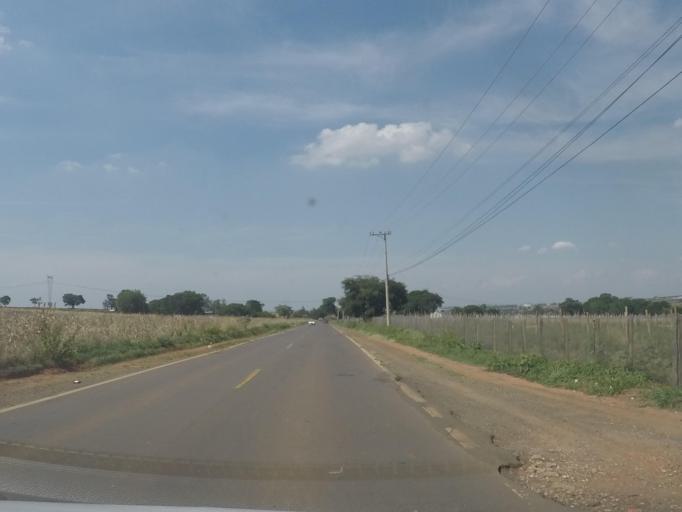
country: BR
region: Sao Paulo
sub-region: Sumare
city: Sumare
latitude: -22.8696
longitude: -47.2974
